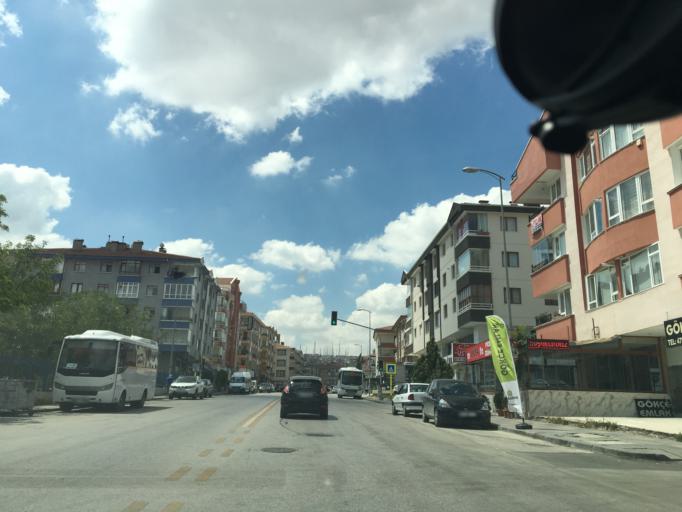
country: TR
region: Ankara
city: Ankara
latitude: 39.8882
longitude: 32.8289
